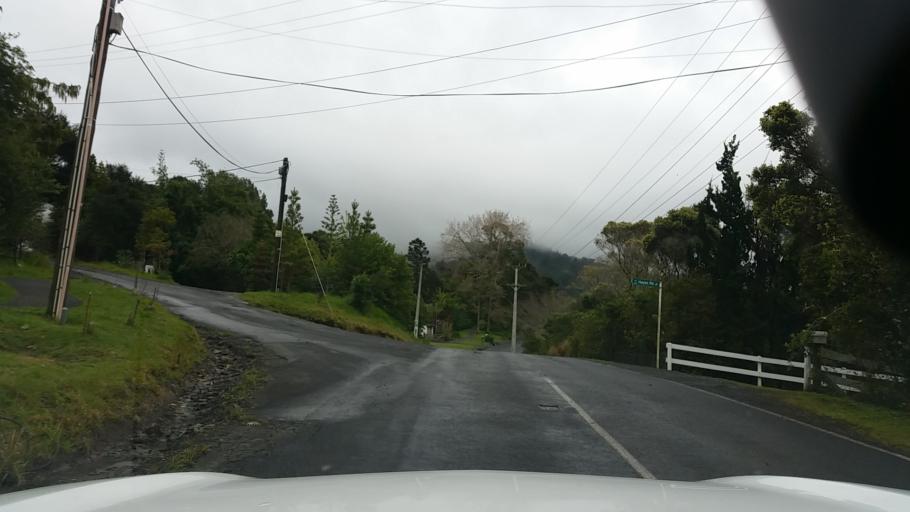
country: NZ
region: Auckland
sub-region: Auckland
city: Waitakere
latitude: -36.9006
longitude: 174.5720
